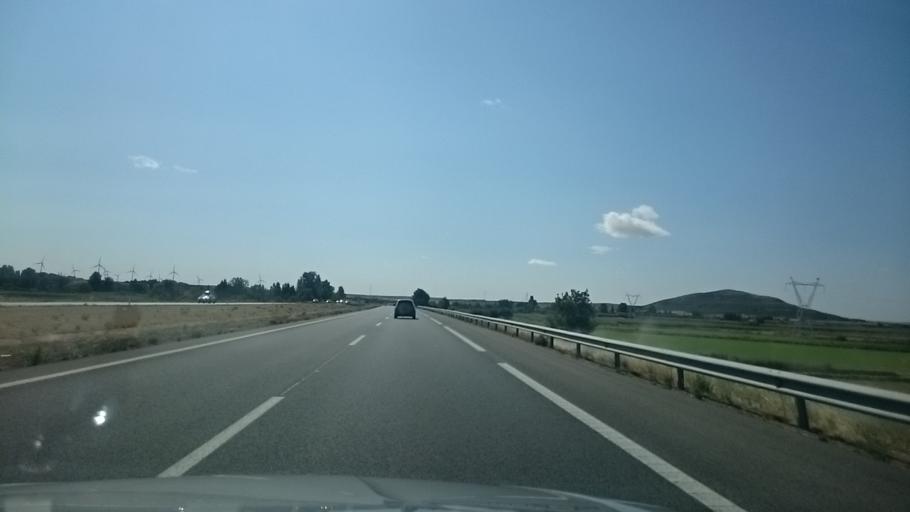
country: ES
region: Aragon
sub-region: Provincia de Zaragoza
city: Frescano
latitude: 41.8984
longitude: -1.4402
